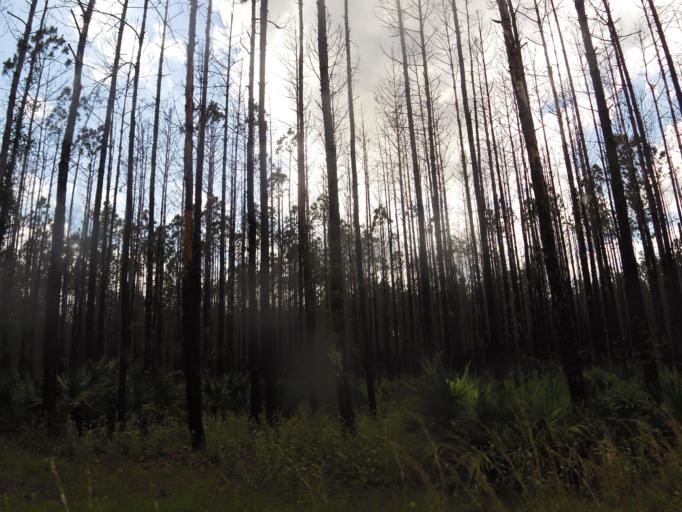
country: US
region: Florida
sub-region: Clay County
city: Keystone Heights
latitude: 29.8540
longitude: -81.8536
